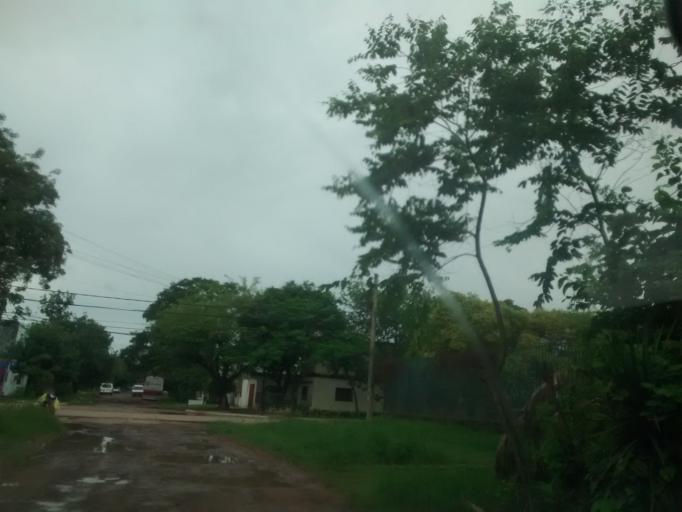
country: AR
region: Chaco
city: Resistencia
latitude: -27.4412
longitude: -58.9823
